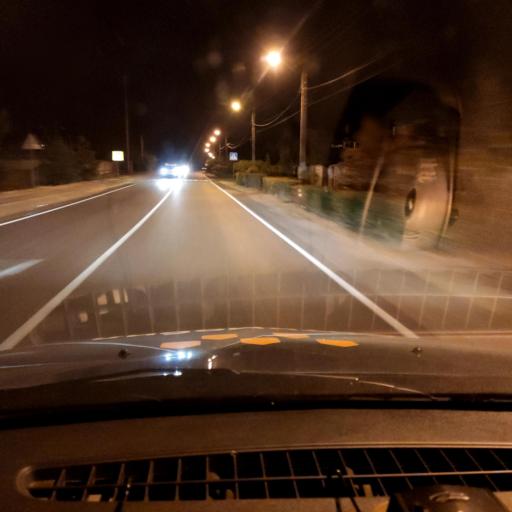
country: RU
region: Voronezj
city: Shilovo
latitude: 51.6026
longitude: 39.0350
